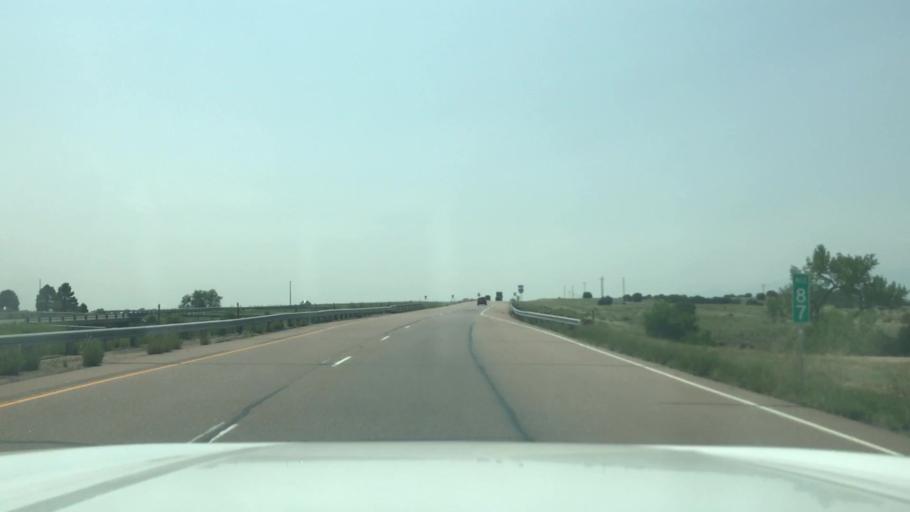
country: US
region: Colorado
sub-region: Pueblo County
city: Pueblo
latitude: 38.1152
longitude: -104.6733
